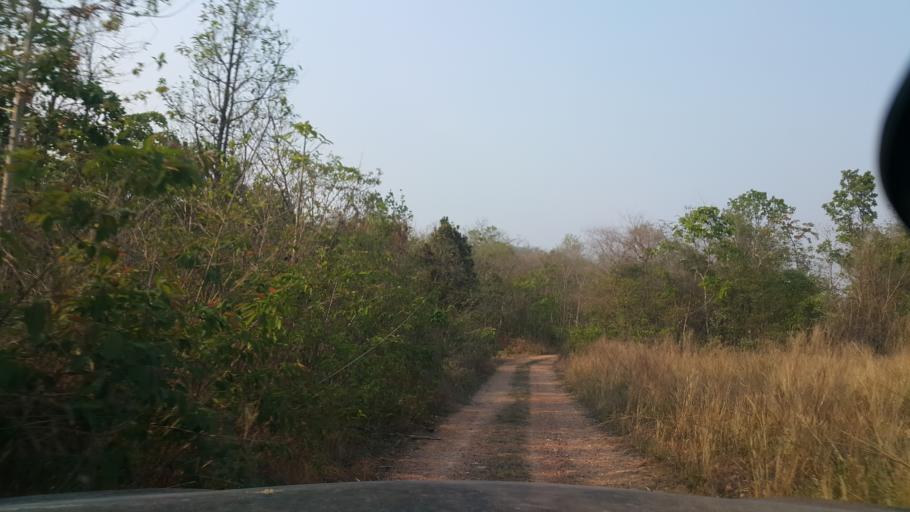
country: TH
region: Sukhothai
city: Thung Saliam
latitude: 17.3364
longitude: 99.4672
